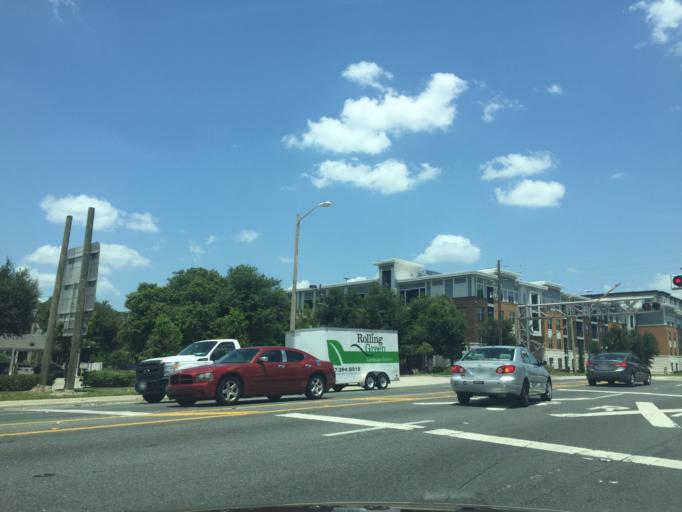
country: US
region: Florida
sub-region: Orange County
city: Orlando
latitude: 28.5530
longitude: -81.3815
